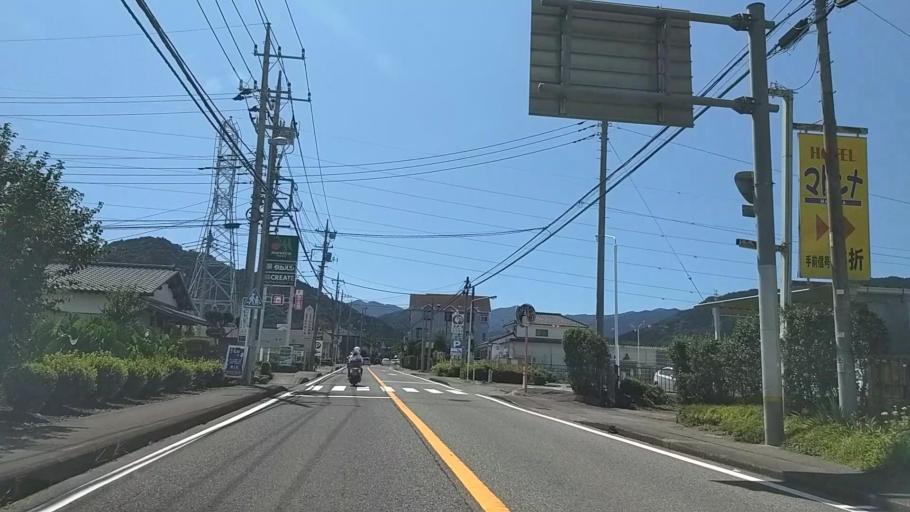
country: JP
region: Tokyo
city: Hachioji
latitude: 35.5866
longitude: 139.2317
